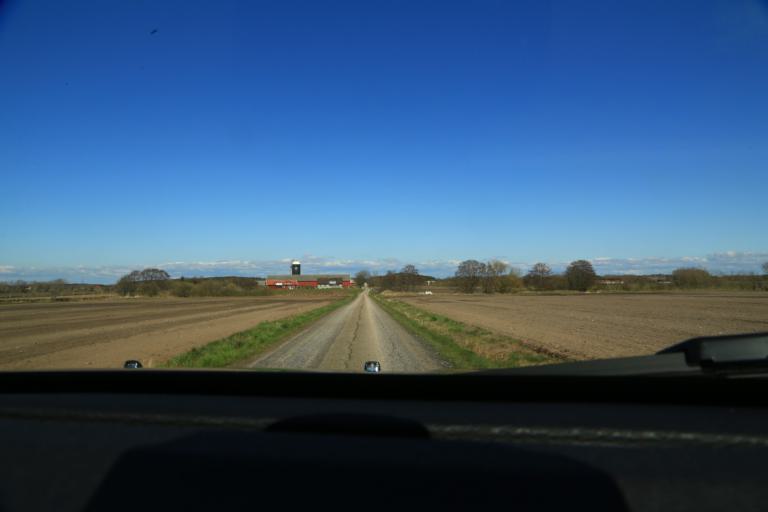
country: SE
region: Halland
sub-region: Varbergs Kommun
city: Traslovslage
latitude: 57.0668
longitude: 12.2990
